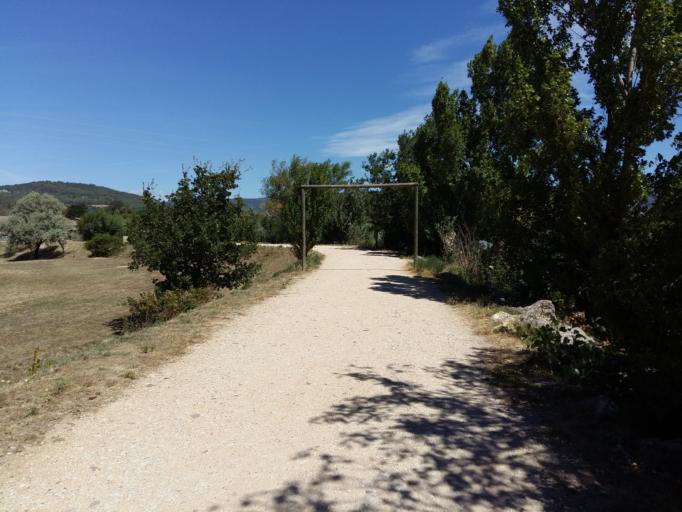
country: FR
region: Provence-Alpes-Cote d'Azur
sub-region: Departement du Vaucluse
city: Apt
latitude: 43.8901
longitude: 5.3780
